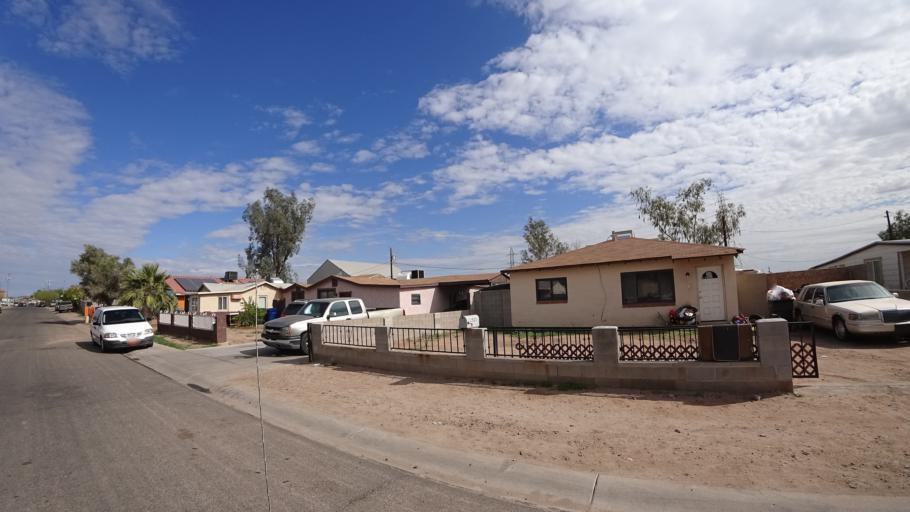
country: US
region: Arizona
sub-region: Maricopa County
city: Phoenix
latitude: 33.4226
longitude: -112.0812
